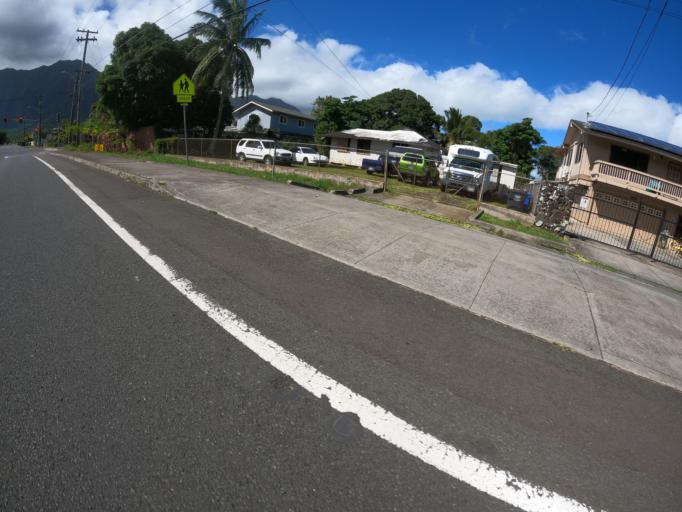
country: US
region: Hawaii
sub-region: Honolulu County
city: Kane'ohe
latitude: 21.4056
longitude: -157.7935
